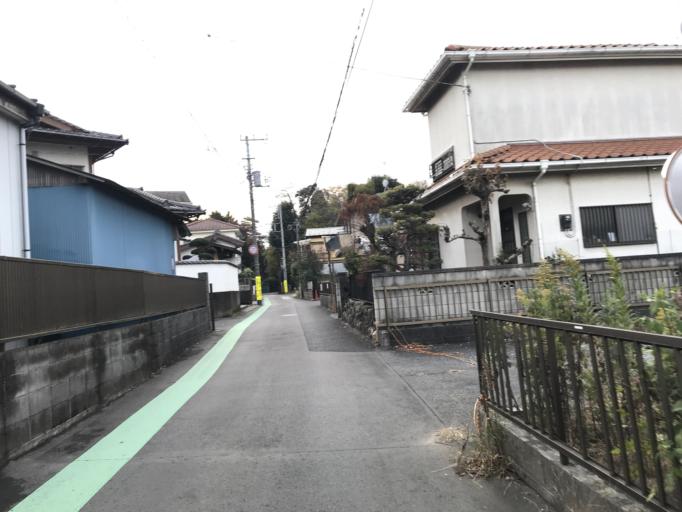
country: JP
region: Chiba
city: Shiroi
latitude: 35.7598
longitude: 140.0121
